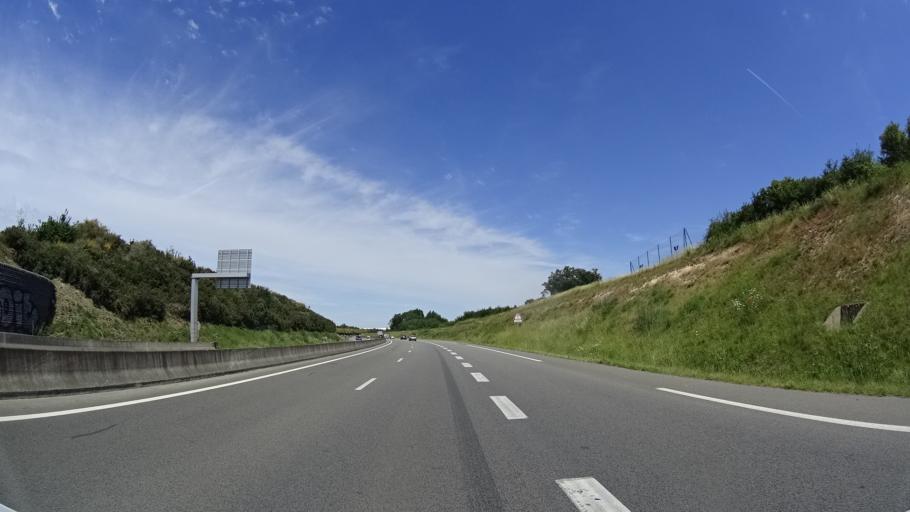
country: FR
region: Pays de la Loire
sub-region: Departement de Maine-et-Loire
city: Beaucouze
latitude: 47.4740
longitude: -0.6169
